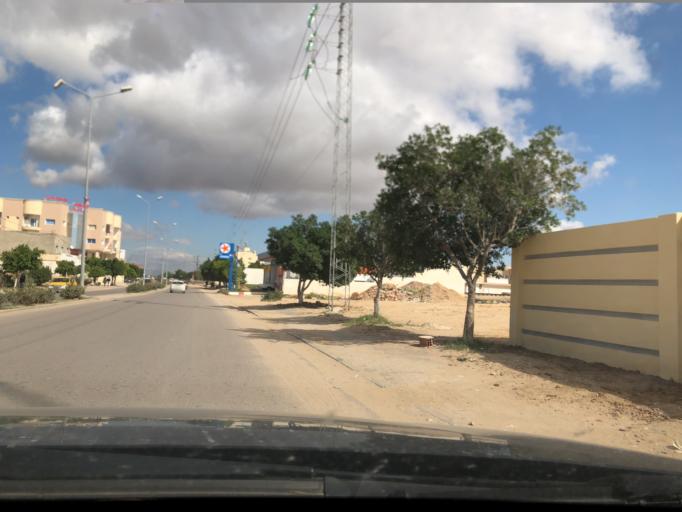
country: TN
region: Al Qasrayn
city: Kasserine
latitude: 35.1733
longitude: 8.8451
